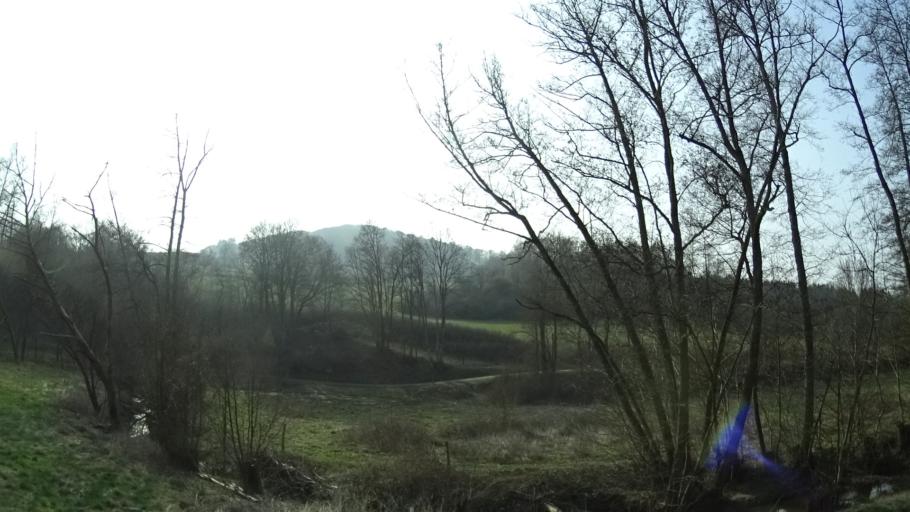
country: DE
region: Rheinland-Pfalz
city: Niederstaufenbach
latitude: 49.5346
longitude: 7.5108
